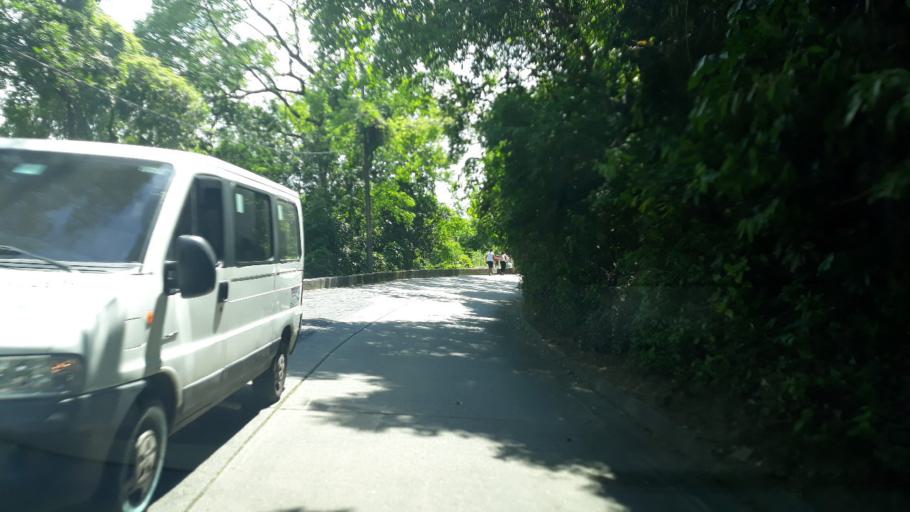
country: BR
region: Rio de Janeiro
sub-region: Rio De Janeiro
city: Rio de Janeiro
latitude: -22.9449
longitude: -43.2056
